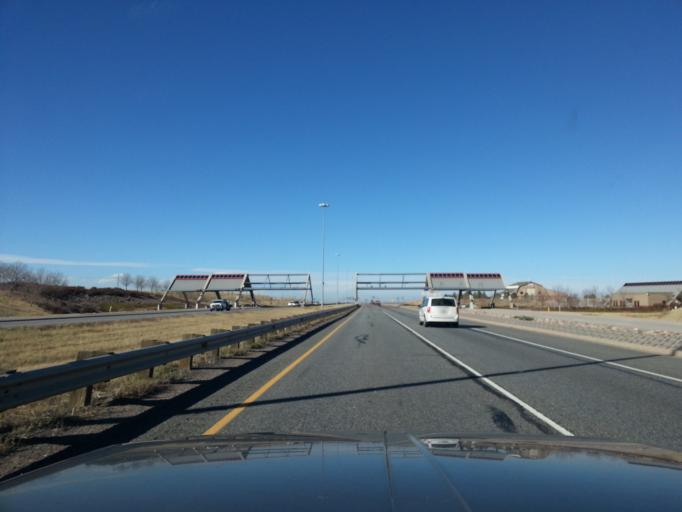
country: US
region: Colorado
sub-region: Adams County
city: Brighton
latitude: 39.8598
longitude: -104.7491
